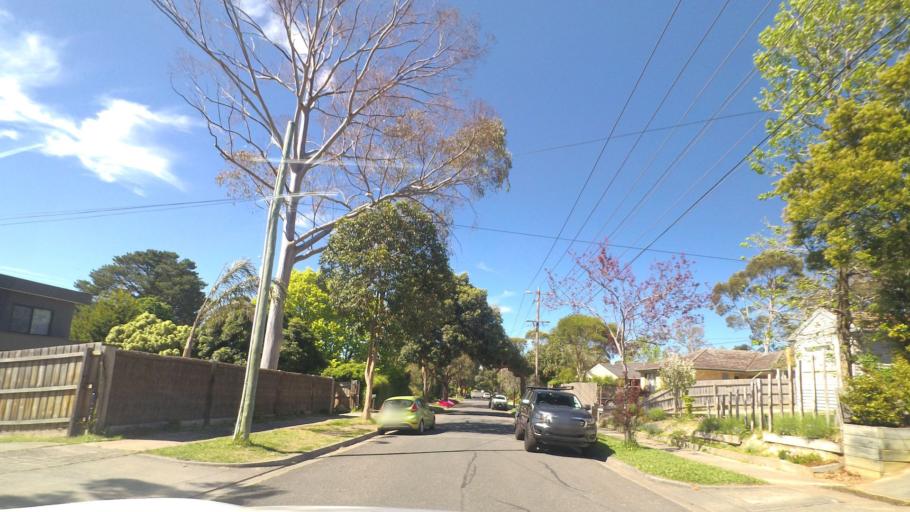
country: AU
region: Victoria
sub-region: Maroondah
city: Ringwood East
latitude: -37.8224
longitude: 145.2592
